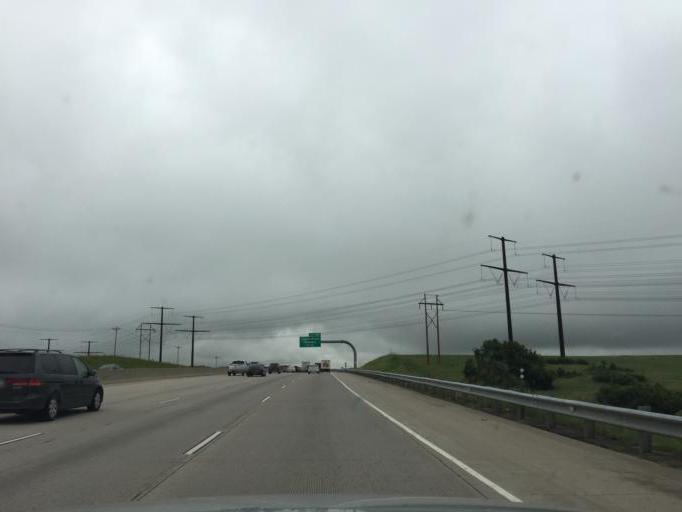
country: US
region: Colorado
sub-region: Douglas County
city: Castle Pines
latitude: 39.4563
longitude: -104.8750
